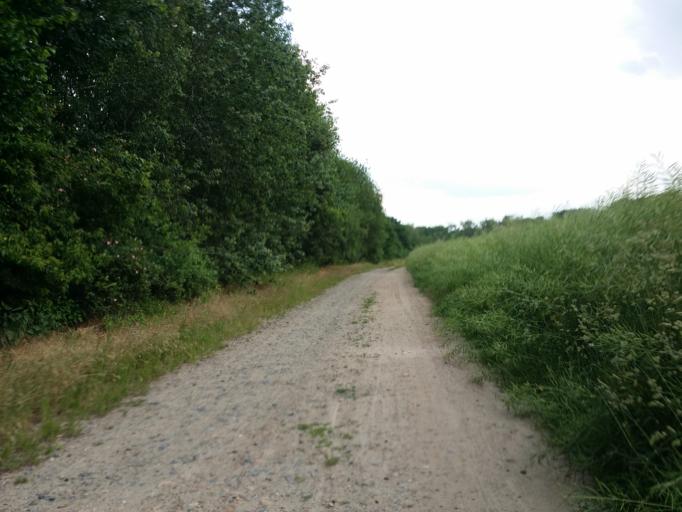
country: DE
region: Lower Saxony
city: Ganderkesee
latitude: 53.0376
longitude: 8.5828
